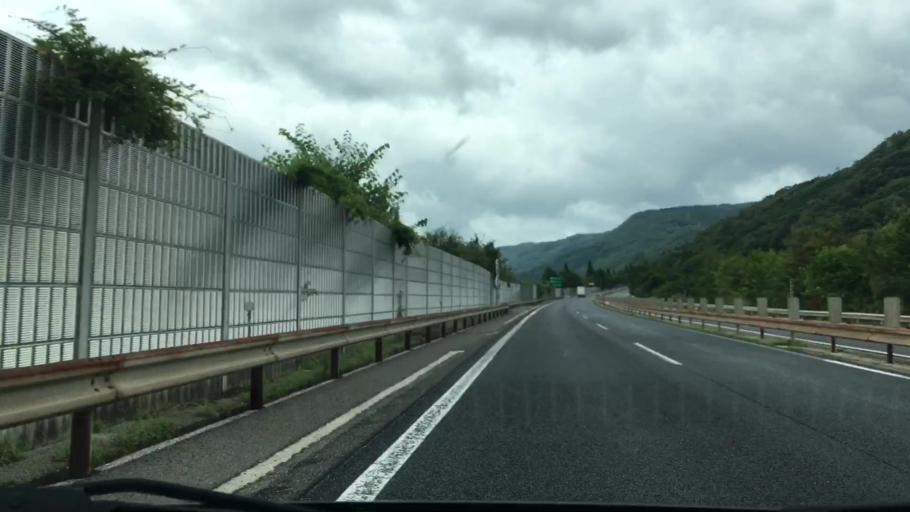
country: JP
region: Okayama
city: Niimi
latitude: 34.9697
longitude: 133.6489
